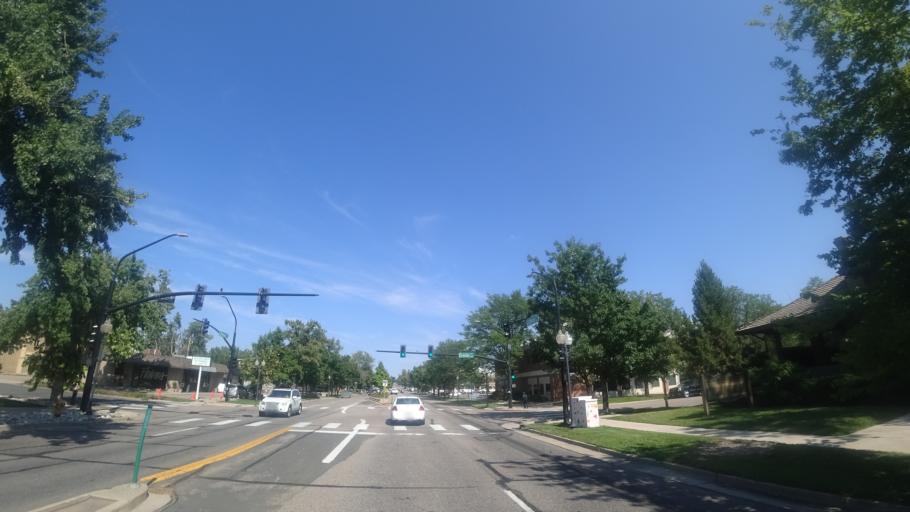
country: US
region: Colorado
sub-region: Arapahoe County
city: Littleton
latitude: 39.6132
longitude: -105.0096
